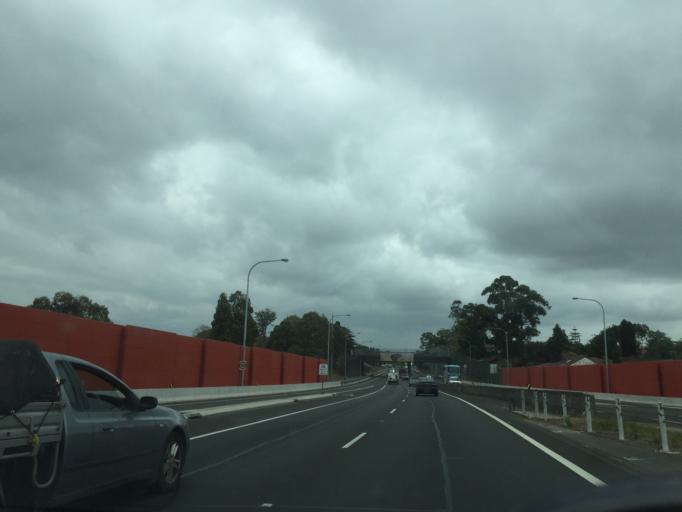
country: AU
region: New South Wales
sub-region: The Hills Shire
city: Baulkham Hills
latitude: -33.7688
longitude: 150.9946
